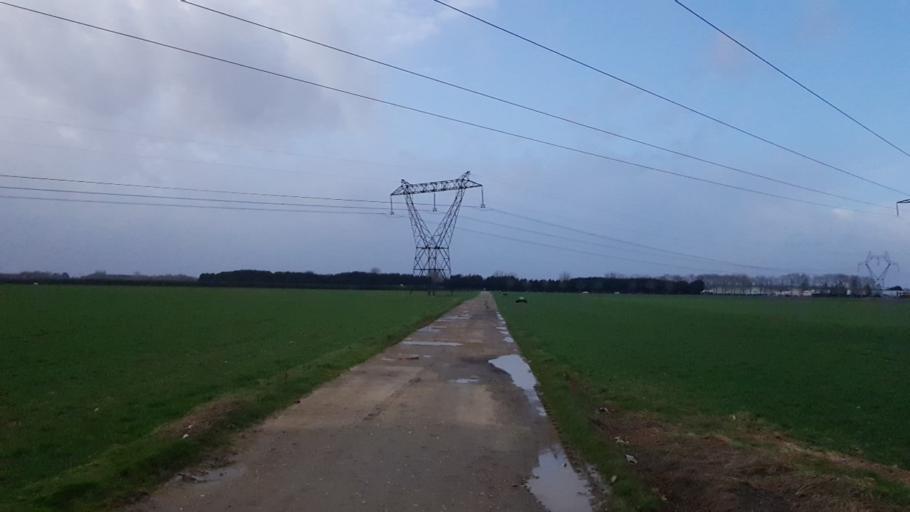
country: FR
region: Ile-de-France
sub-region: Departement de l'Essonne
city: Cheptainville
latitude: 48.5619
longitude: 2.2796
